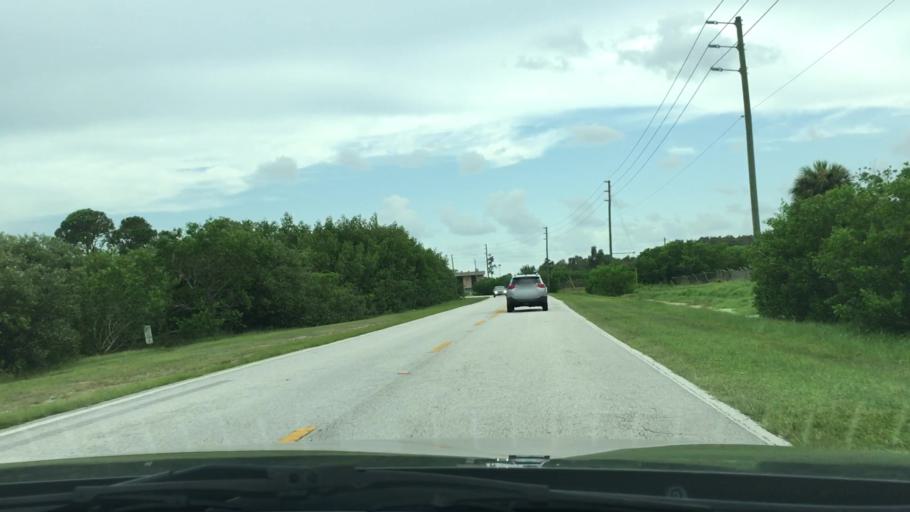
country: US
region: Florida
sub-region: Pinellas County
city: Gandy
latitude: 27.8618
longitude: -82.6252
